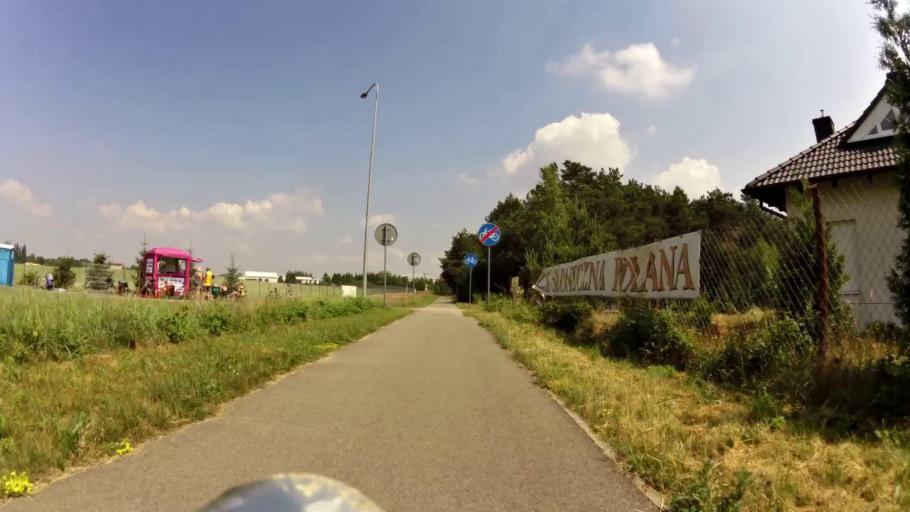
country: PL
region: Kujawsko-Pomorskie
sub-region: Powiat bydgoski
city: Koronowo
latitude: 53.2805
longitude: 17.9350
